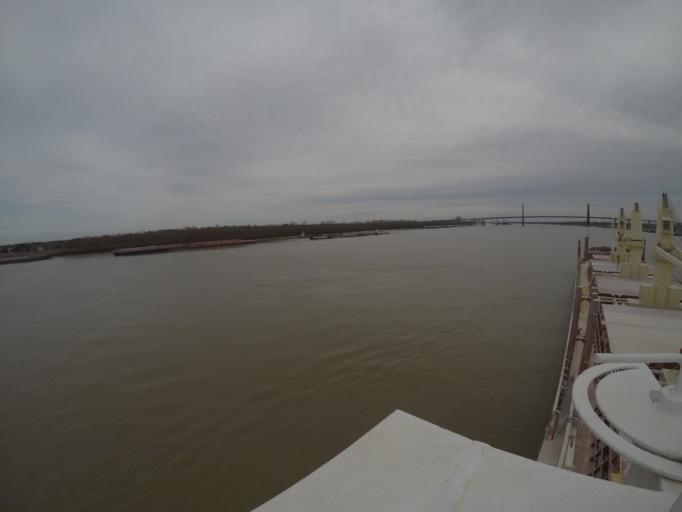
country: US
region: Louisiana
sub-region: Saint Charles Parish
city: New Sarpy
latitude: 29.9499
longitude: -90.3909
